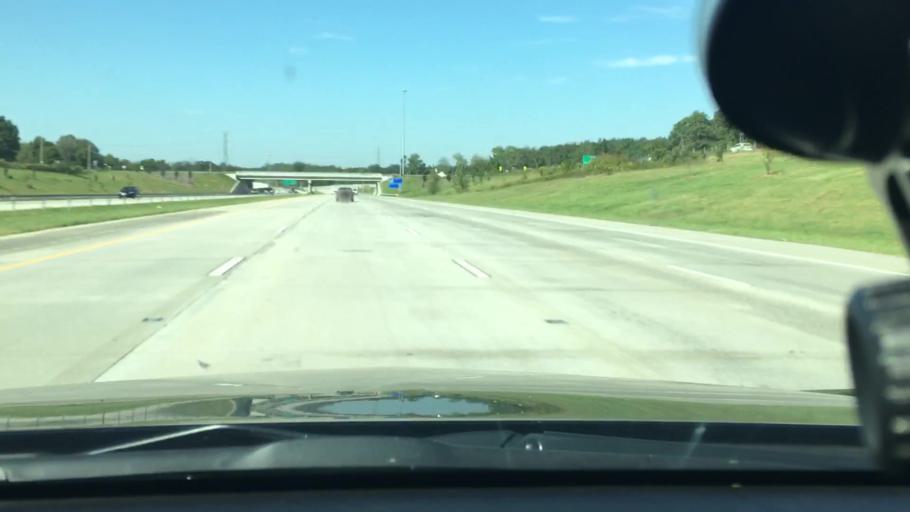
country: US
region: North Carolina
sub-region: Mecklenburg County
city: Huntersville
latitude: 35.3691
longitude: -80.7856
